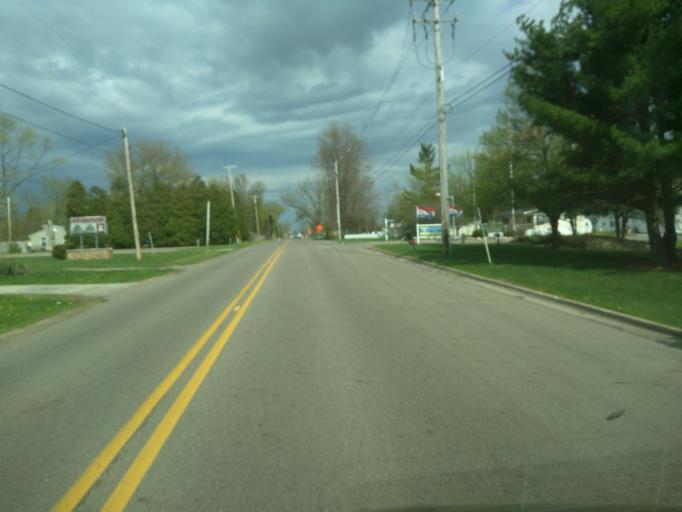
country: US
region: Michigan
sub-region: Eaton County
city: Dimondale
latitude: 42.6831
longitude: -84.6093
